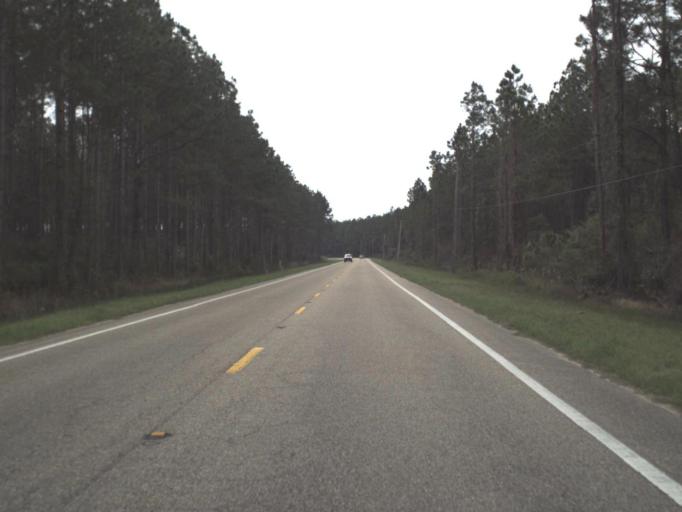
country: US
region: Florida
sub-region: Gulf County
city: Port Saint Joe
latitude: 29.8399
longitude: -85.2702
